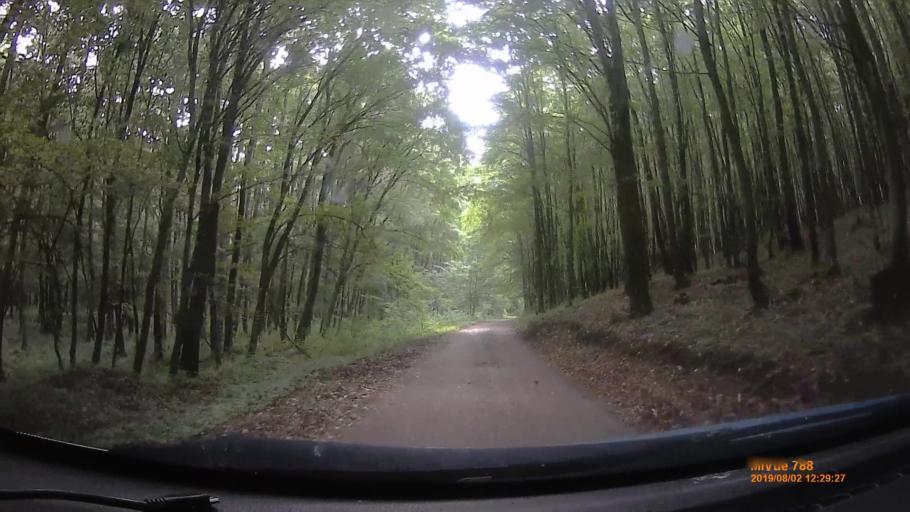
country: HU
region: Baranya
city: Buekkoesd
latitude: 46.1122
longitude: 17.9356
